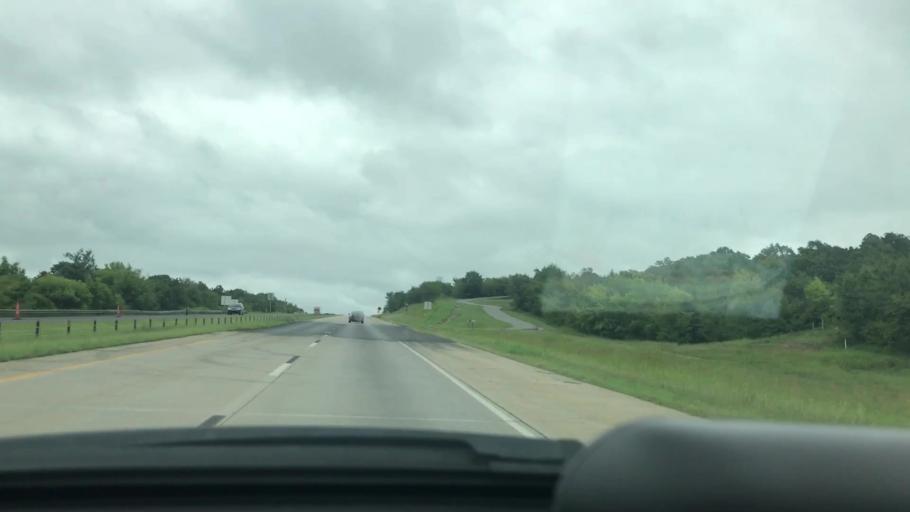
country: US
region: Oklahoma
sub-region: Pittsburg County
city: Krebs
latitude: 34.9649
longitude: -95.7243
